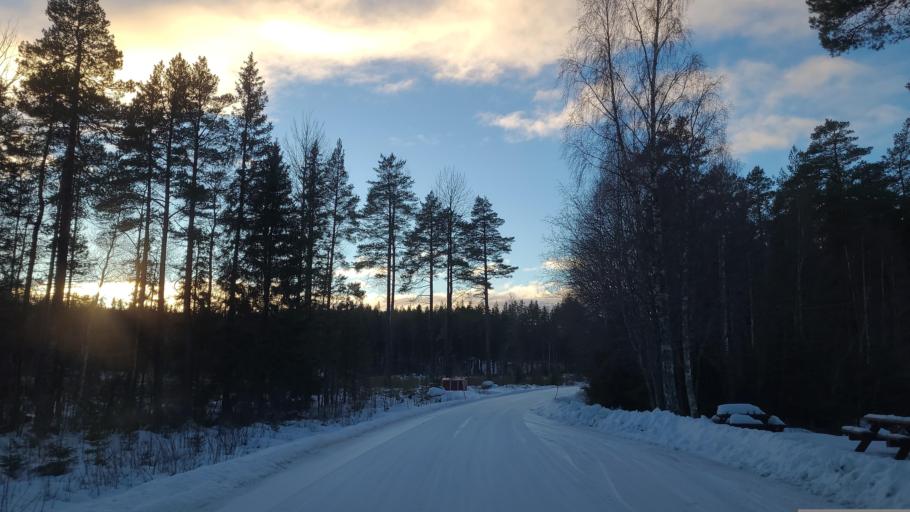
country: SE
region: Gaevleborg
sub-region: Bollnas Kommun
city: Kilafors
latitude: 61.3851
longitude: 16.6923
